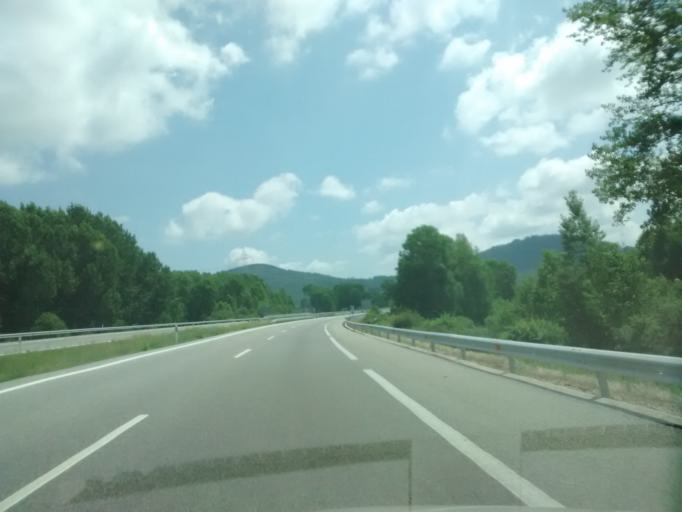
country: ES
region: Castille and Leon
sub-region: Provincia de Leon
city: Ponferrada
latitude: 42.5829
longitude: -6.6151
